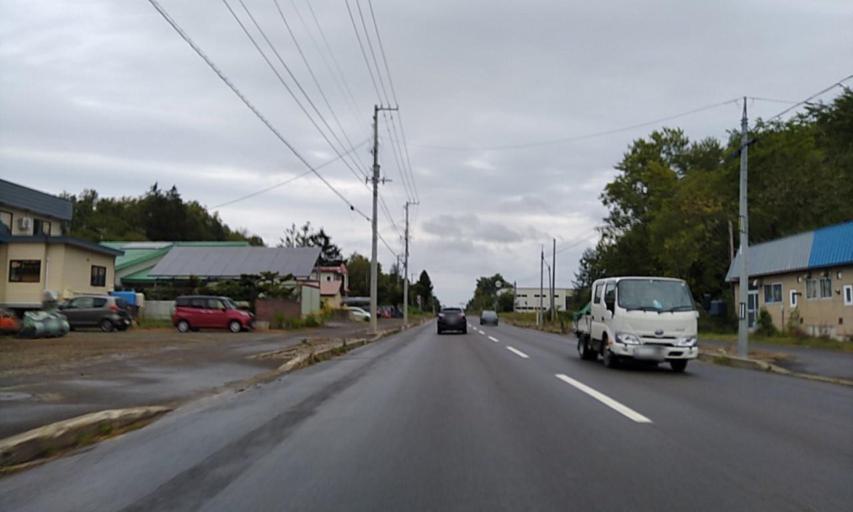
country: JP
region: Hokkaido
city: Kitami
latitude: 44.0825
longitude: 143.9461
